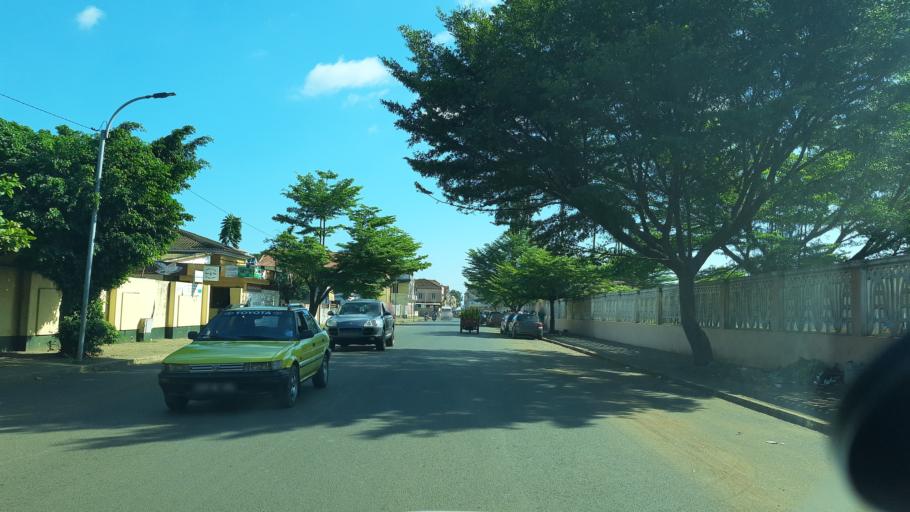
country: ST
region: Sao Tome Island
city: Sao Tome
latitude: 0.3352
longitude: 6.7304
